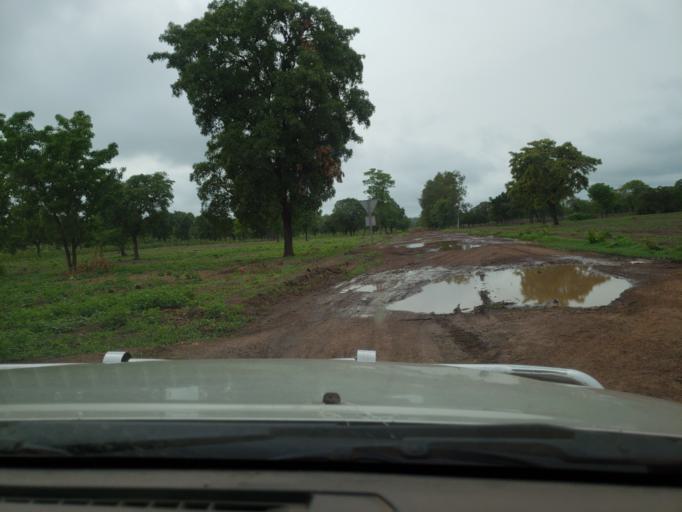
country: ML
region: Koulikoro
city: Kangaba
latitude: 12.0238
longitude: -8.7301
